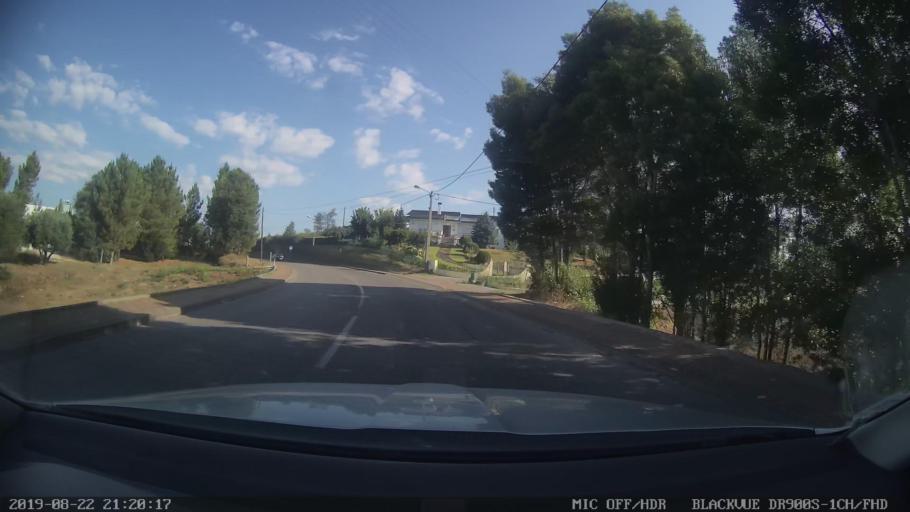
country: PT
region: Castelo Branco
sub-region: Serta
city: Serta
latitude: 39.8113
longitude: -8.1069
